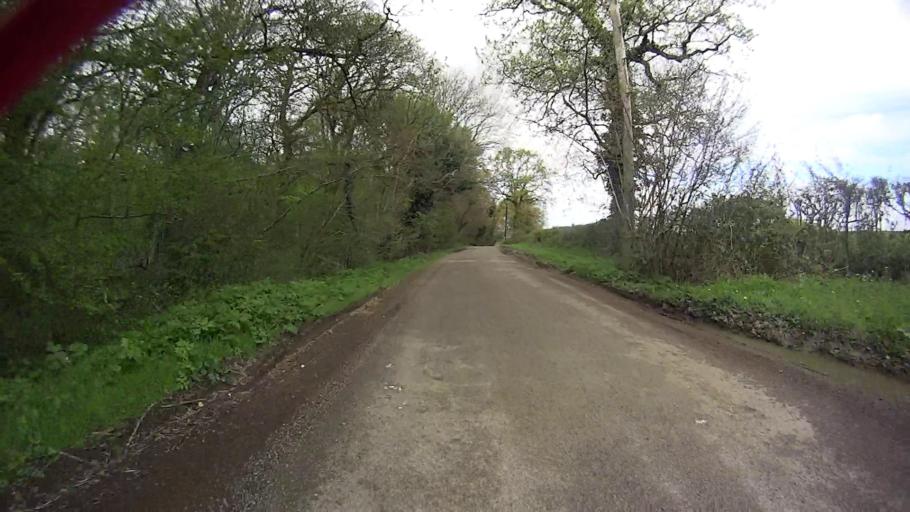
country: GB
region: England
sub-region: West Sussex
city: Horsham
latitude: 51.1076
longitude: -0.3022
